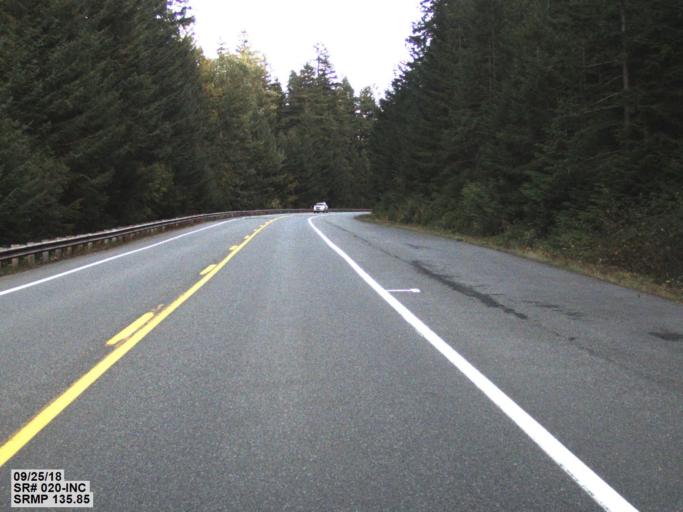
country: US
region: Washington
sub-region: Snohomish County
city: Darrington
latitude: 48.7245
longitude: -121.0271
